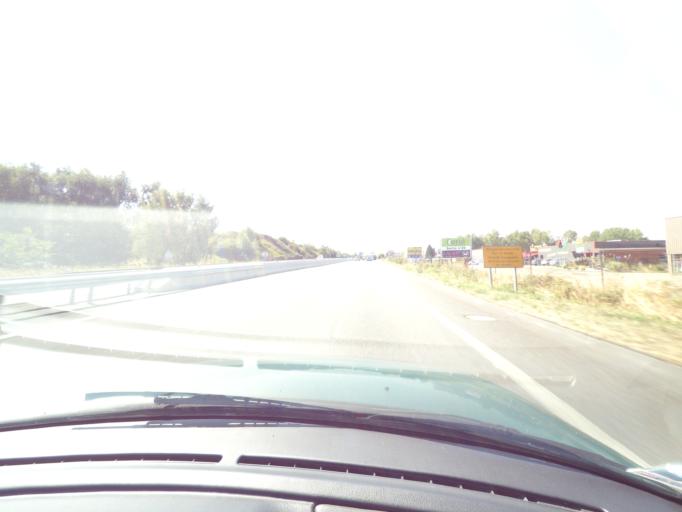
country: FR
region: Limousin
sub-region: Departement de la Haute-Vienne
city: Rilhac-Rancon
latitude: 45.8882
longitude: 1.2924
